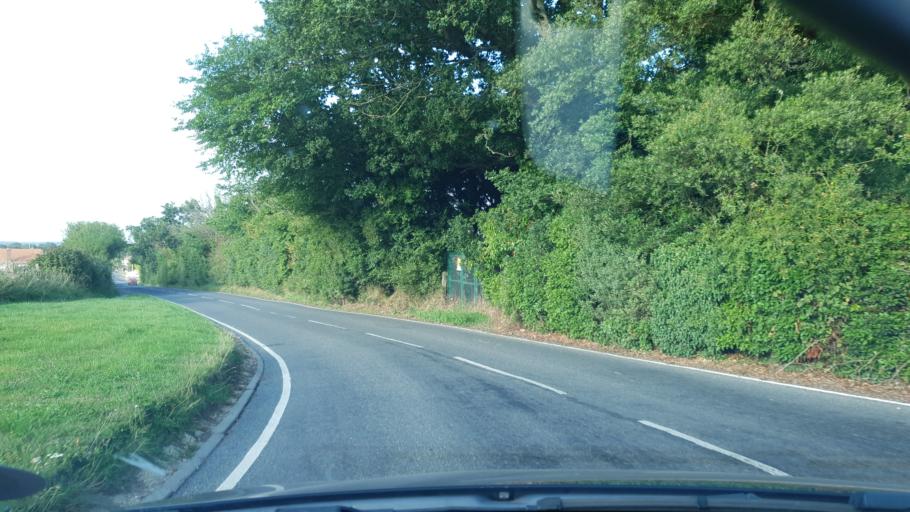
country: GB
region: England
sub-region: Essex
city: Frinton-on-Sea
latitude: 51.8482
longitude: 1.2232
